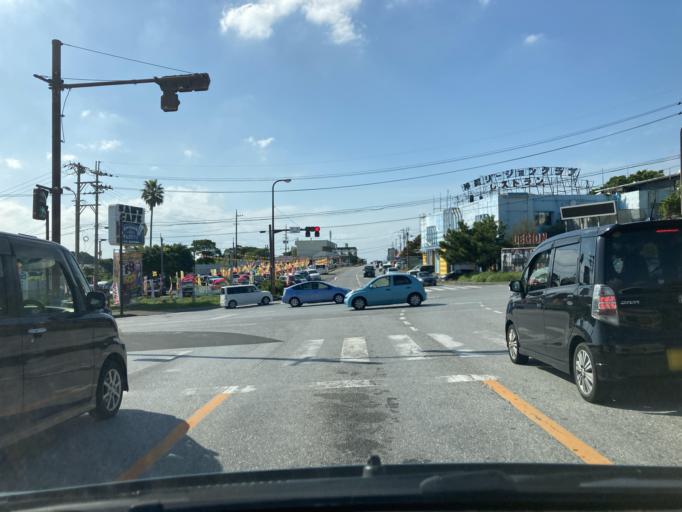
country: JP
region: Okinawa
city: Chatan
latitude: 26.2964
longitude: 127.7808
